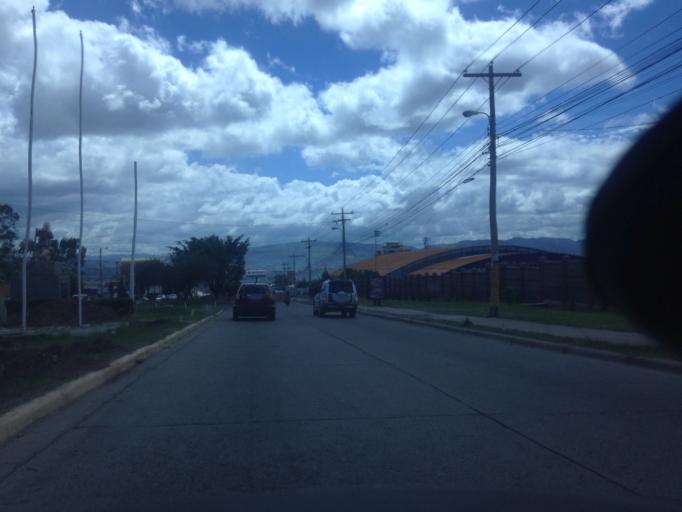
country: HN
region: Francisco Morazan
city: Tegucigalpa
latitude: 14.0836
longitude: -87.1675
